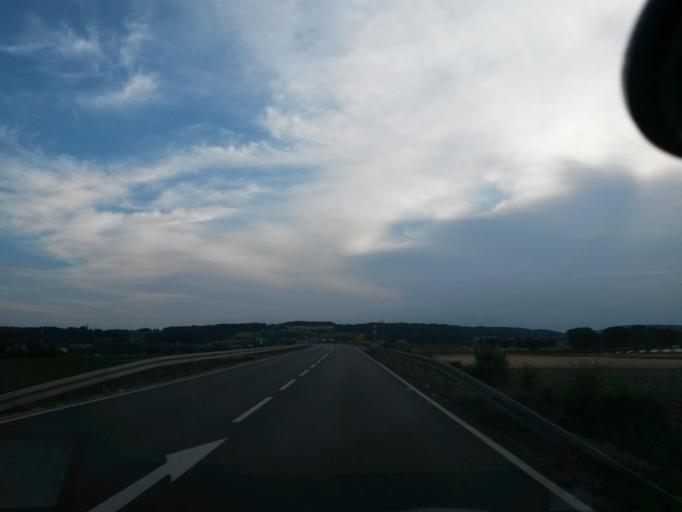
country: DE
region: Bavaria
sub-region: Upper Palatinate
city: Amberg
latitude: 49.4774
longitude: 11.8568
